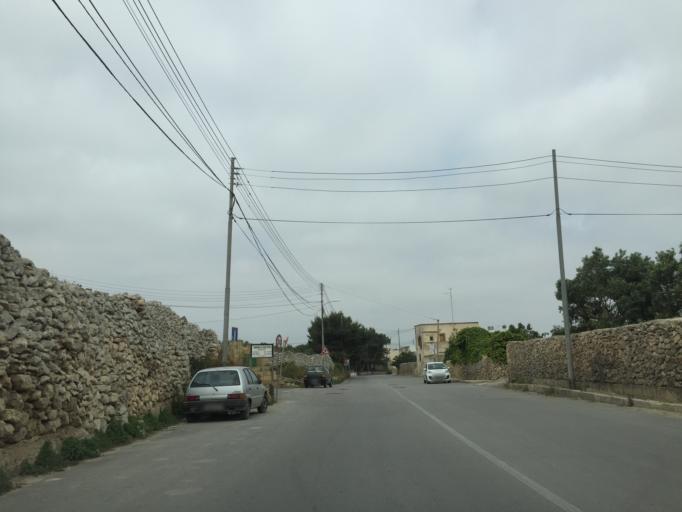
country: MT
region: Ir-Rabat
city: Rabat
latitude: 35.8844
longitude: 14.3887
